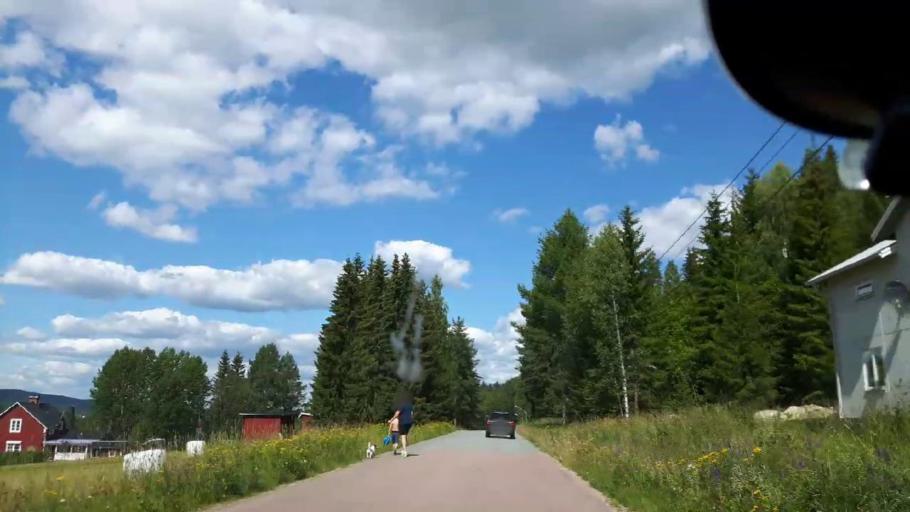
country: SE
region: Jaemtland
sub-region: Ragunda Kommun
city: Hammarstrand
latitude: 62.9452
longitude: 16.6899
